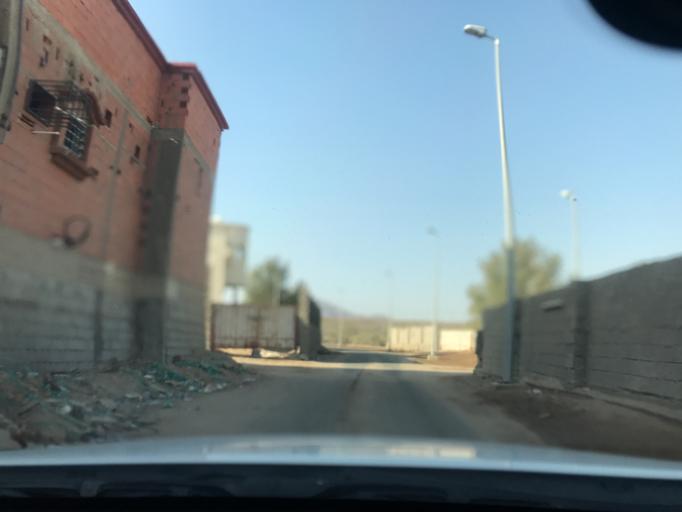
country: SA
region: Makkah
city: Al Jumum
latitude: 21.4523
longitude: 39.5352
